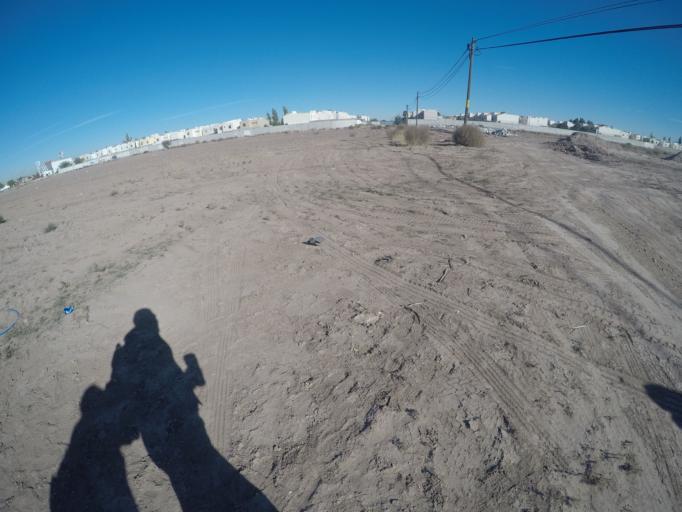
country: US
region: Texas
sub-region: El Paso County
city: Socorro
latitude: 31.6983
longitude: -106.3799
